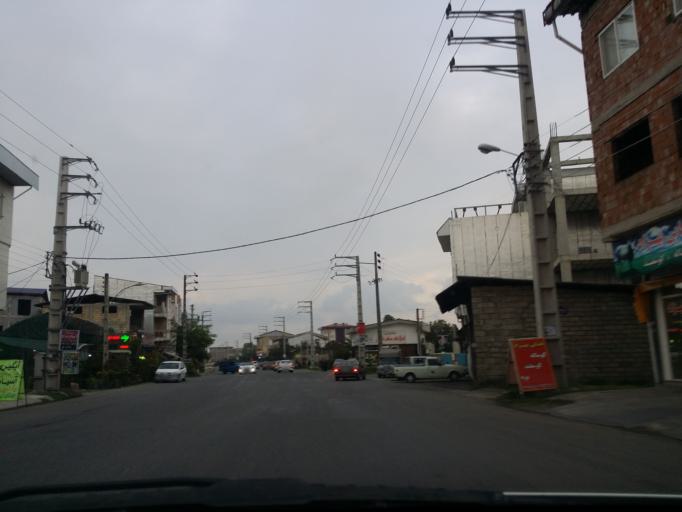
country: IR
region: Mazandaran
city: `Abbasabad
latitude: 36.7124
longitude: 51.1014
